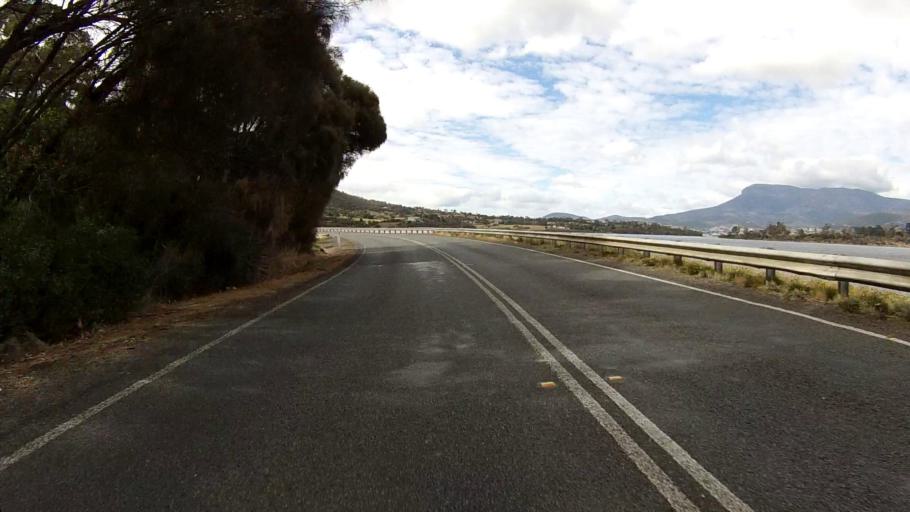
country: AU
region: Tasmania
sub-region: Brighton
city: Old Beach
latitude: -42.7816
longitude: 147.2859
